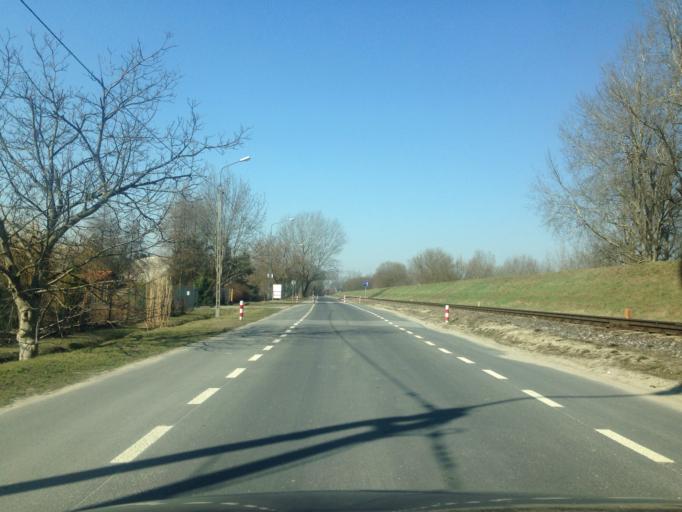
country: PL
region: Masovian Voivodeship
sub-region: Warszawa
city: Wilanow
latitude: 52.1635
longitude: 21.1310
